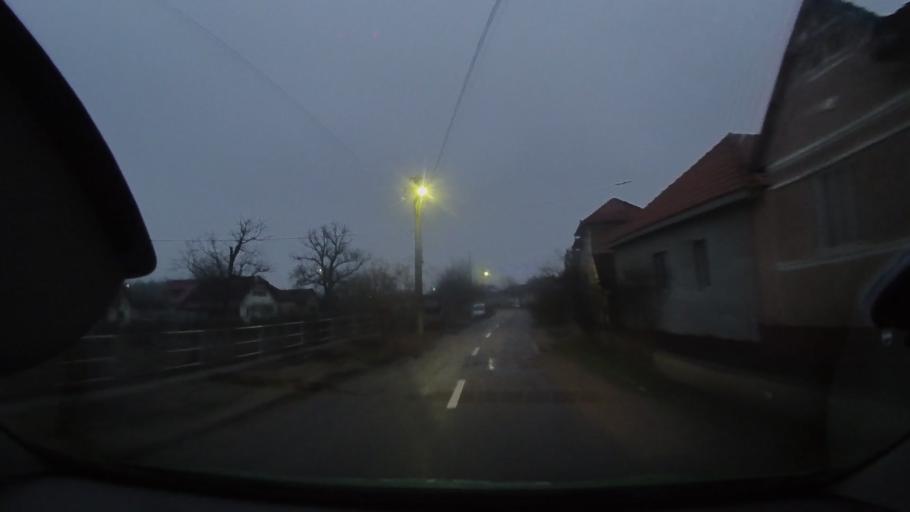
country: RO
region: Arad
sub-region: Comuna Archis
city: Archis
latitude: 46.4775
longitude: 22.0463
